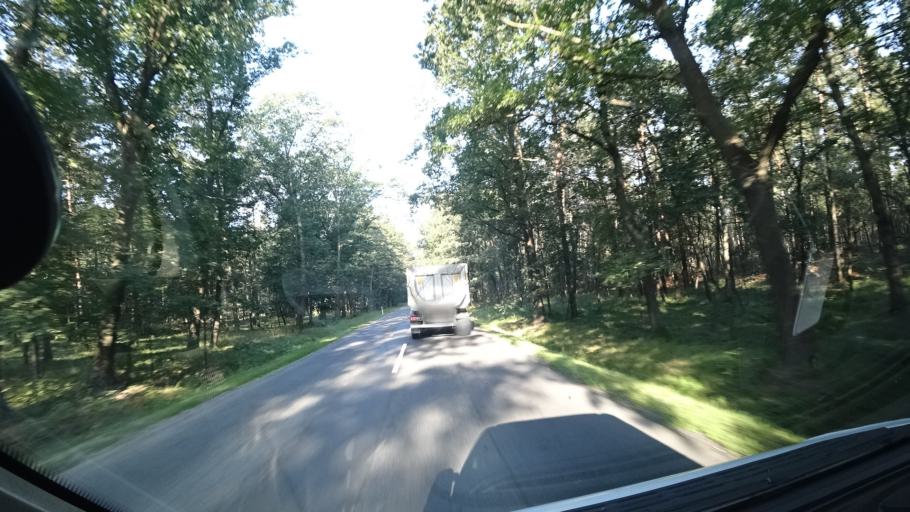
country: PL
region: Silesian Voivodeship
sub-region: Powiat gliwicki
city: Rudziniec
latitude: 50.2743
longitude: 18.3874
